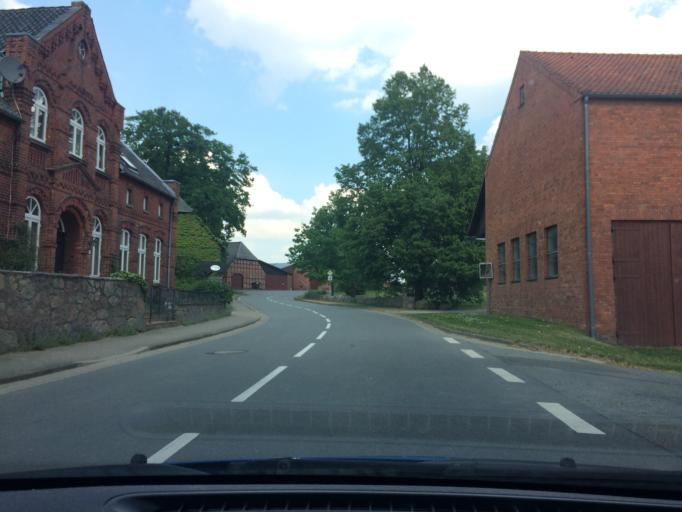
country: DE
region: Lower Saxony
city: Tosterglope
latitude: 53.2088
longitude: 10.8209
